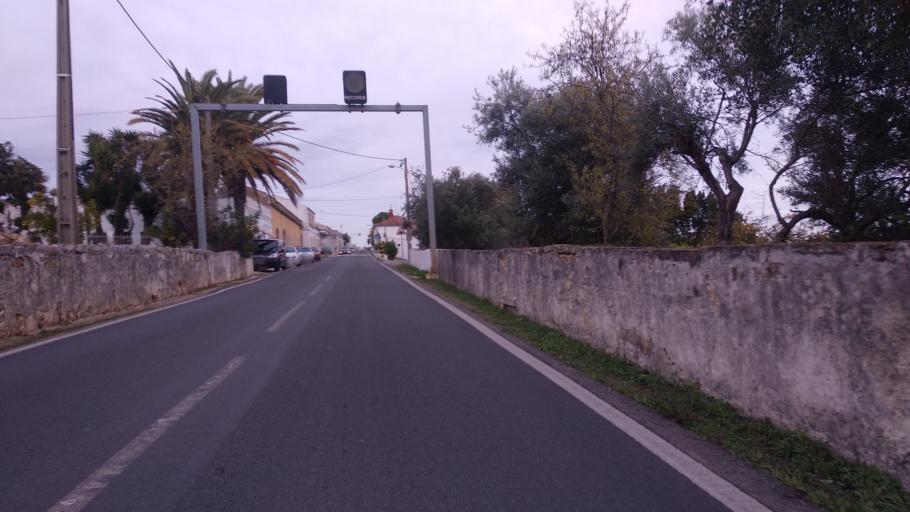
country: PT
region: Faro
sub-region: Sao Bras de Alportel
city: Sao Bras de Alportel
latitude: 37.1519
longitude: -7.9226
